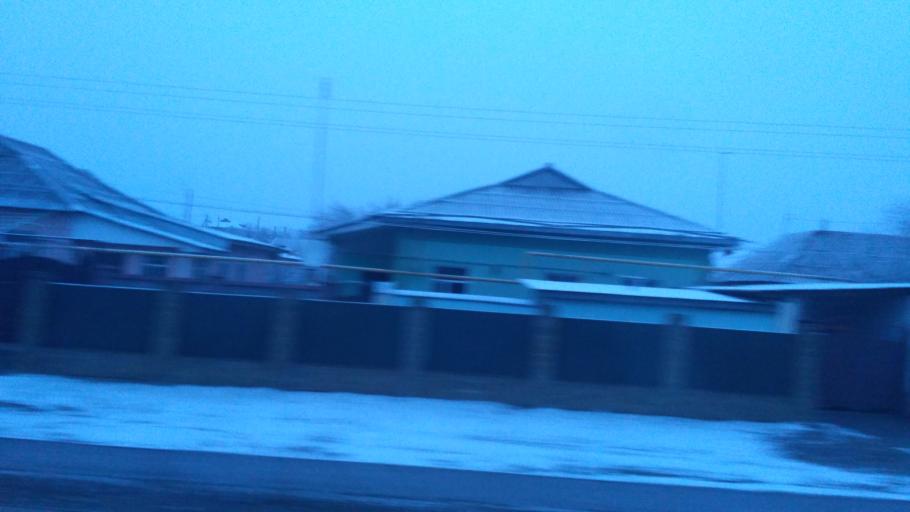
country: KZ
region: Ongtustik Qazaqstan
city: Shymkent
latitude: 42.3711
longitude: 69.5061
